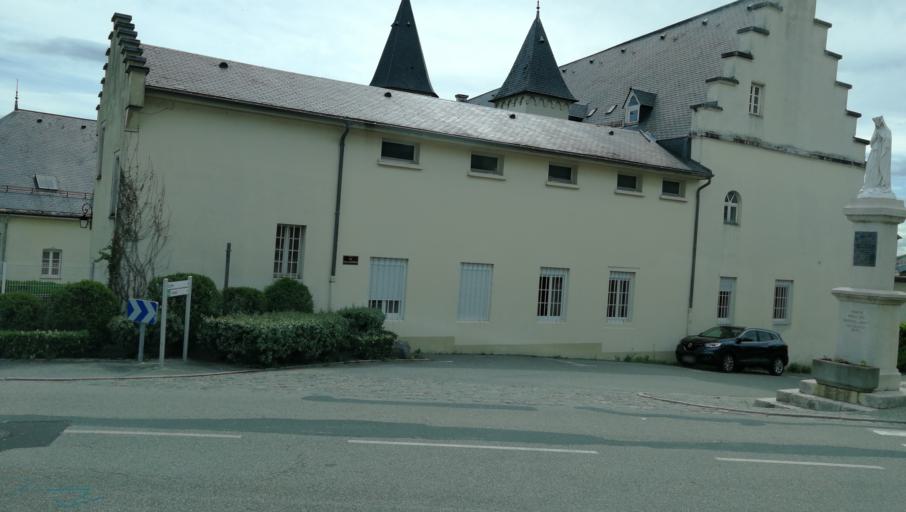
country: FR
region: Rhone-Alpes
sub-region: Departement de l'Ain
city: Bellegarde-sur-Valserine
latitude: 46.0061
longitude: 5.7857
